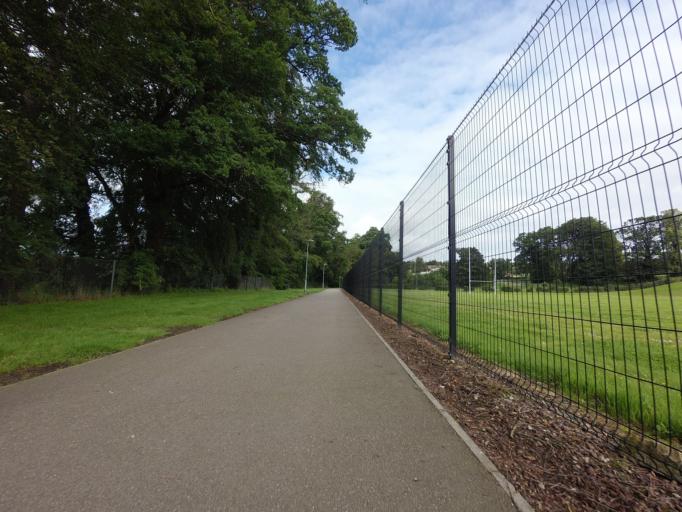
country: GB
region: Scotland
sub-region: Moray
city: Elgin
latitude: 57.6514
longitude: -3.3302
